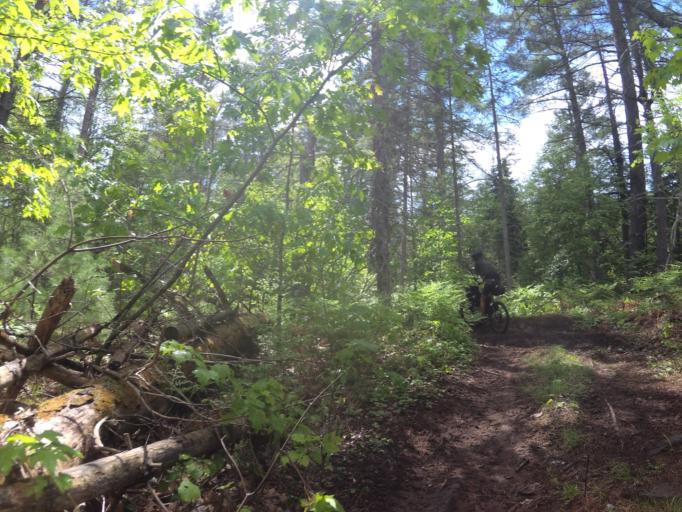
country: CA
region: Ontario
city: Renfrew
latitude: 45.1258
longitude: -76.8426
